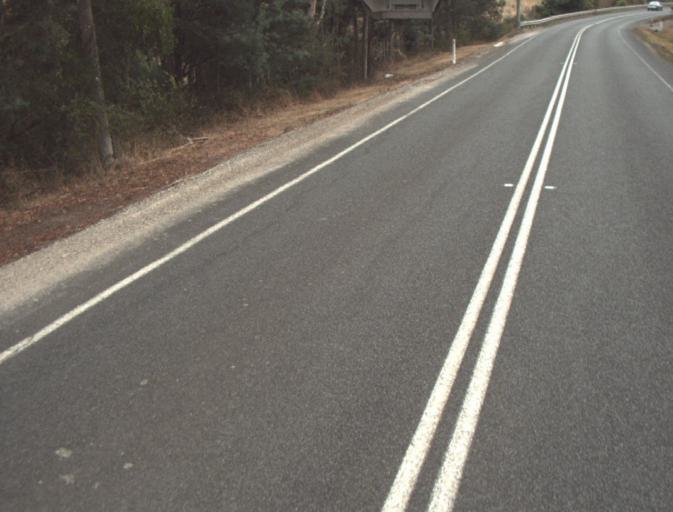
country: AU
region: Tasmania
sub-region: Launceston
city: Mayfield
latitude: -41.2696
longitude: 147.2142
